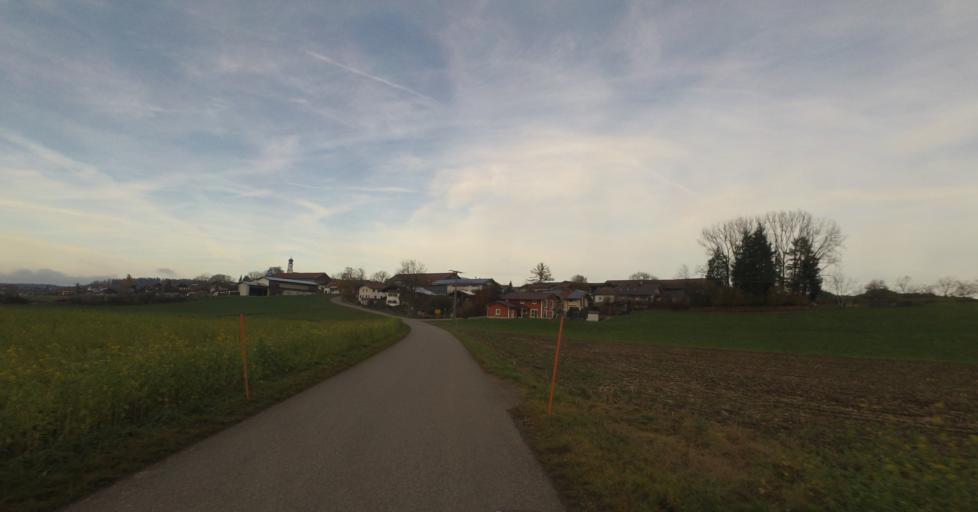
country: DE
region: Bavaria
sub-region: Upper Bavaria
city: Nussdorf
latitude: 47.9017
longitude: 12.5949
